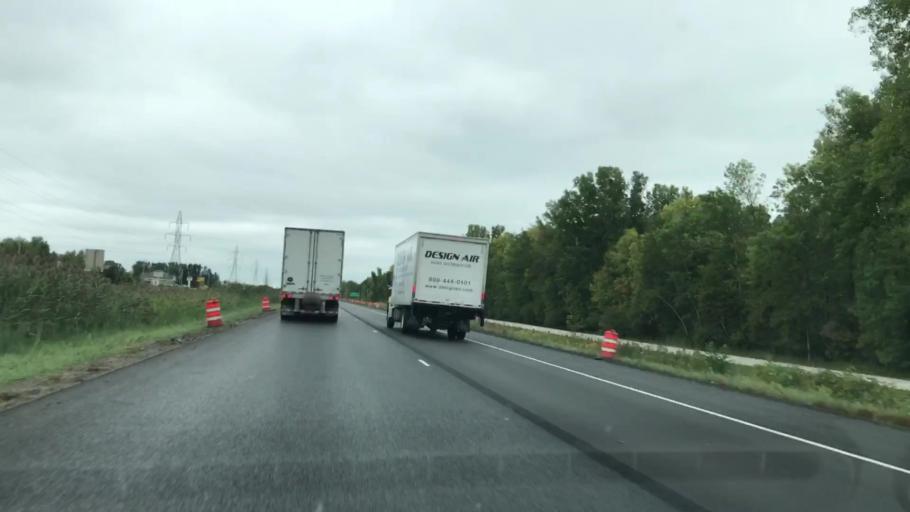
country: US
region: Wisconsin
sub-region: Brown County
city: Suamico
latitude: 44.6125
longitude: -88.0502
